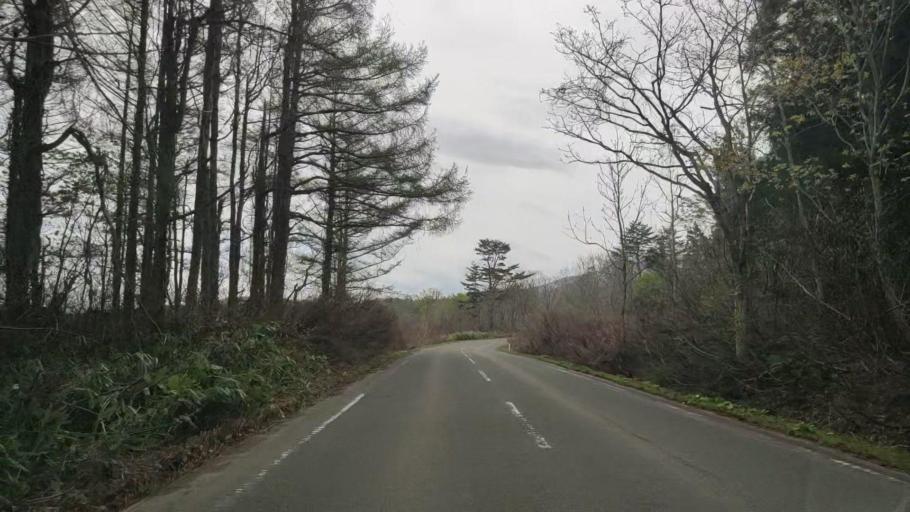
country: JP
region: Aomori
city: Aomori Shi
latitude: 40.7276
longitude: 140.8480
